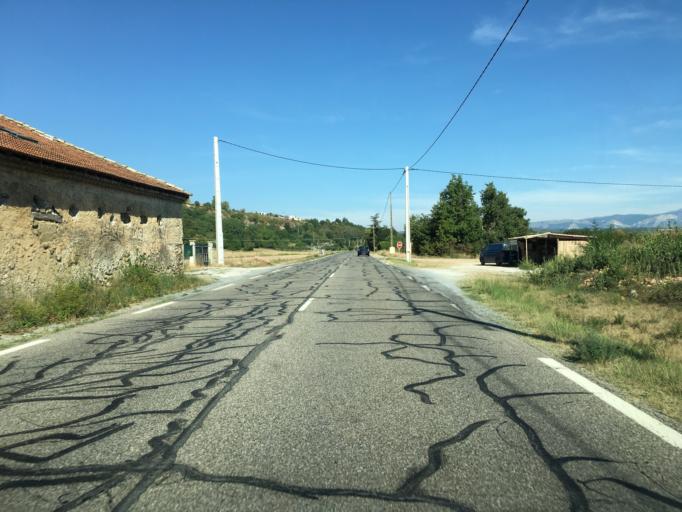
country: FR
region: Provence-Alpes-Cote d'Azur
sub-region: Departement des Alpes-de-Haute-Provence
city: Sisteron
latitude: 44.2419
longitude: 5.8942
